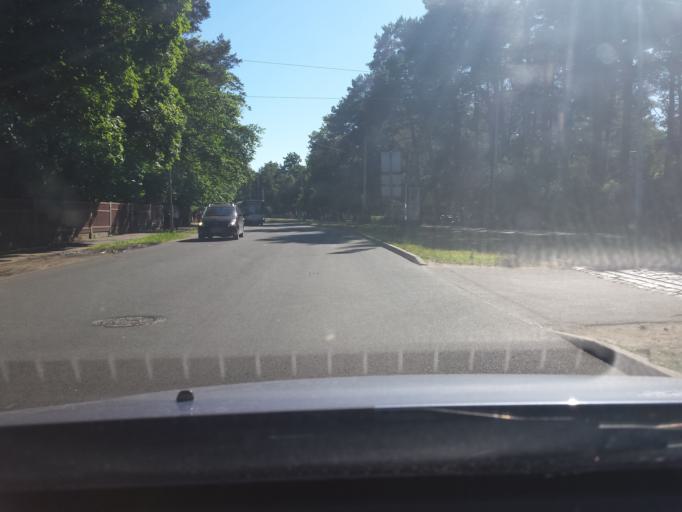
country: LV
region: Riga
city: Jaunciems
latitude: 57.0063
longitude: 24.1591
